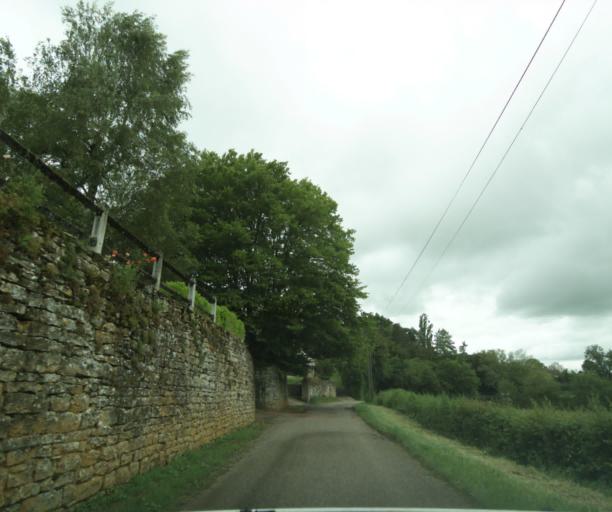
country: FR
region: Bourgogne
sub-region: Departement de Saone-et-Loire
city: Charolles
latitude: 46.4396
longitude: 4.2793
